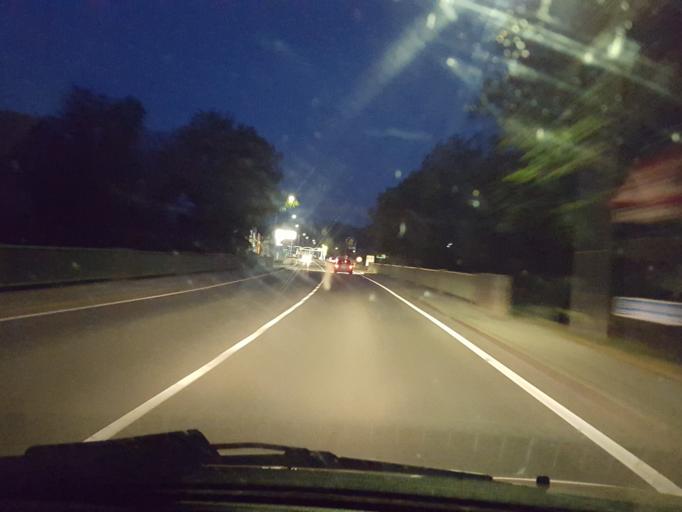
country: AT
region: Lower Austria
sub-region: Politischer Bezirk Scheibbs
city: Purgstall
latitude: 48.0645
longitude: 15.1361
